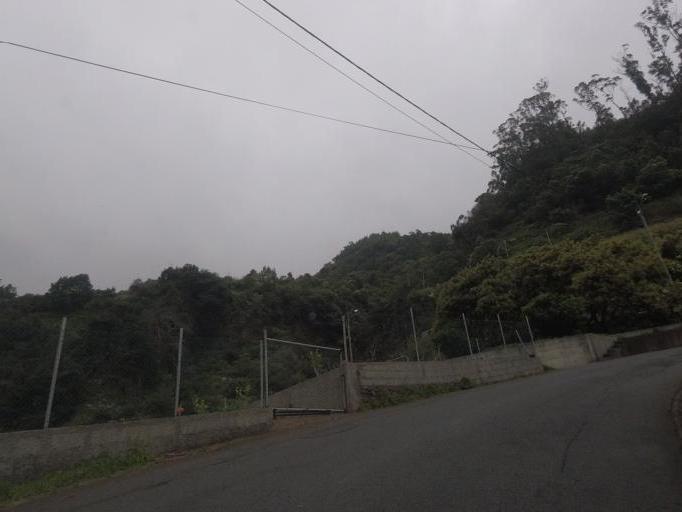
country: PT
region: Madeira
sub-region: Santa Cruz
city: Santa Cruz
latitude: 32.7367
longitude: -16.8087
